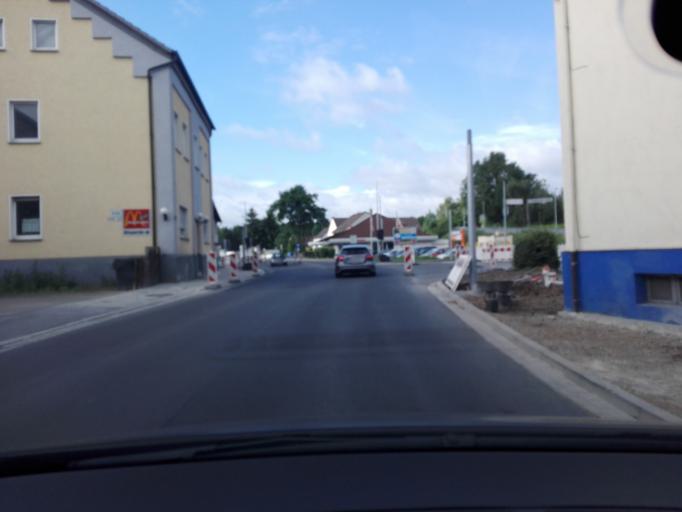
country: DE
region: North Rhine-Westphalia
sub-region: Regierungsbezirk Arnsberg
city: Menden
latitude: 51.4594
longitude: 7.7760
